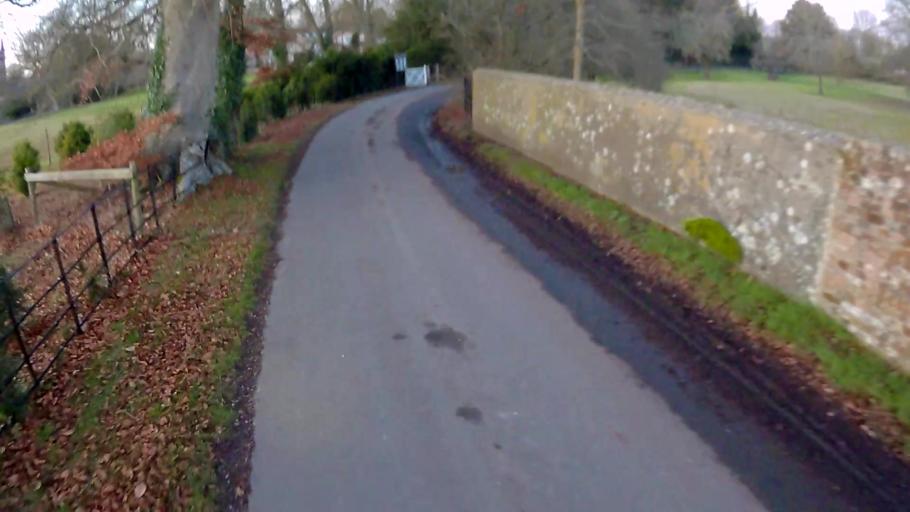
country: GB
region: England
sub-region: Hampshire
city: Overton
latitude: 51.2479
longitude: -1.2177
